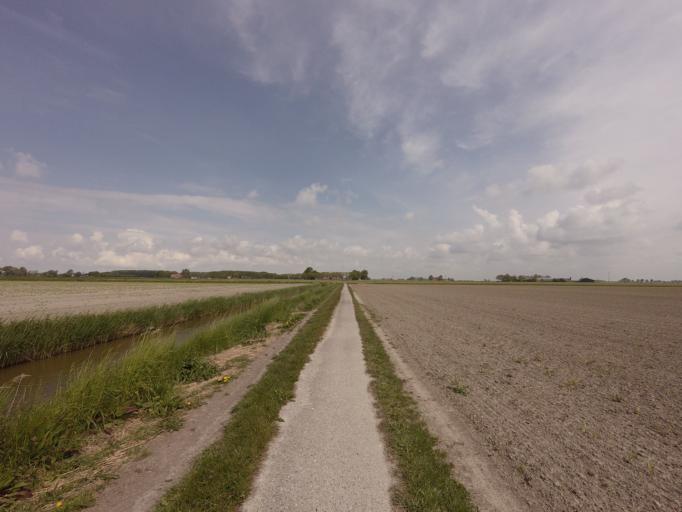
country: NL
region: Friesland
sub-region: Sudwest Fryslan
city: Bolsward
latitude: 53.1055
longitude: 5.4873
